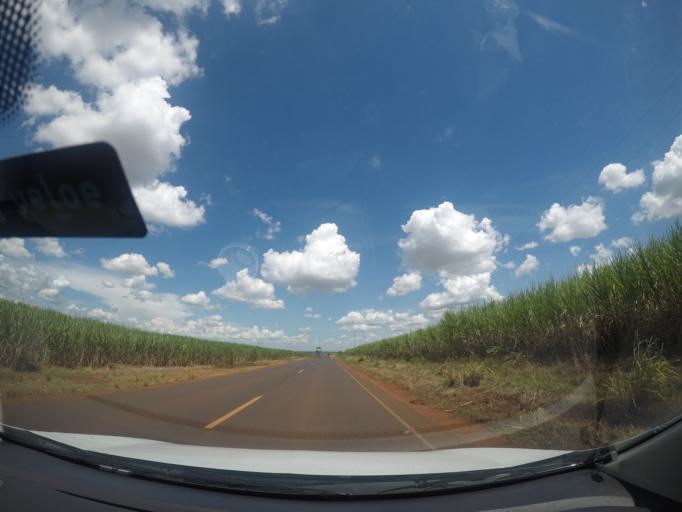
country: BR
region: Minas Gerais
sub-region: Frutal
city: Frutal
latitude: -19.8666
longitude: -48.7289
